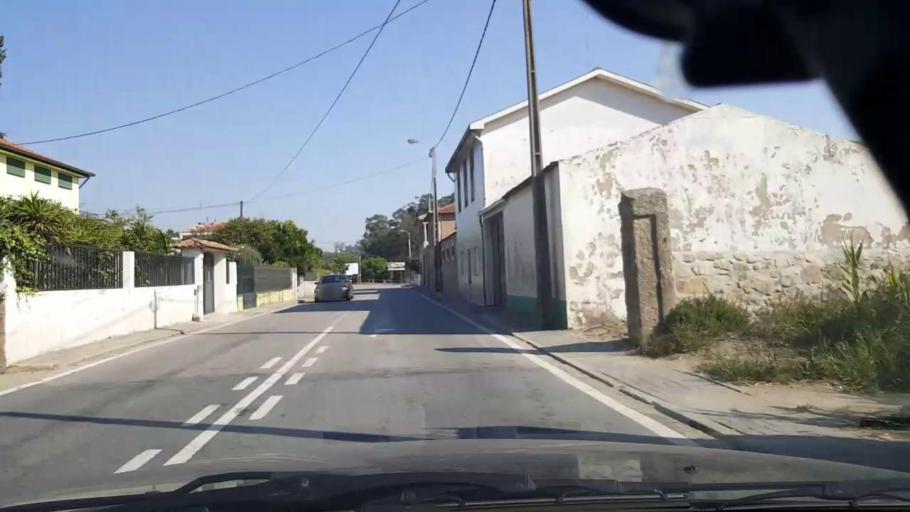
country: PT
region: Porto
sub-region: Vila do Conde
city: Arvore
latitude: 41.3470
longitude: -8.6789
